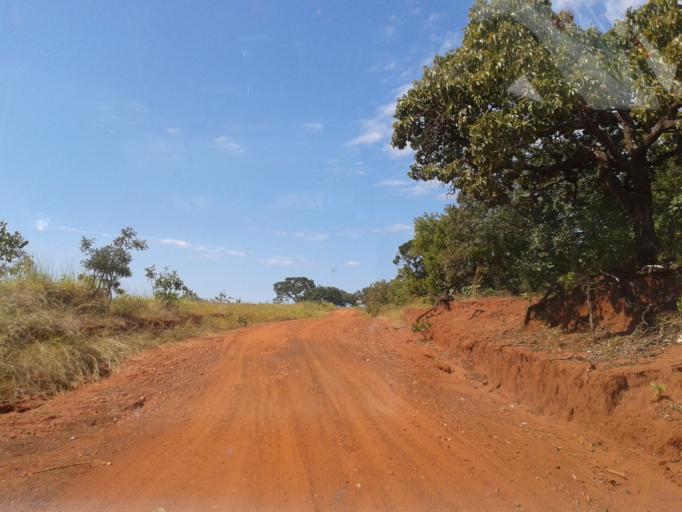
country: BR
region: Minas Gerais
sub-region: Campina Verde
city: Campina Verde
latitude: -19.4017
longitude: -49.7552
